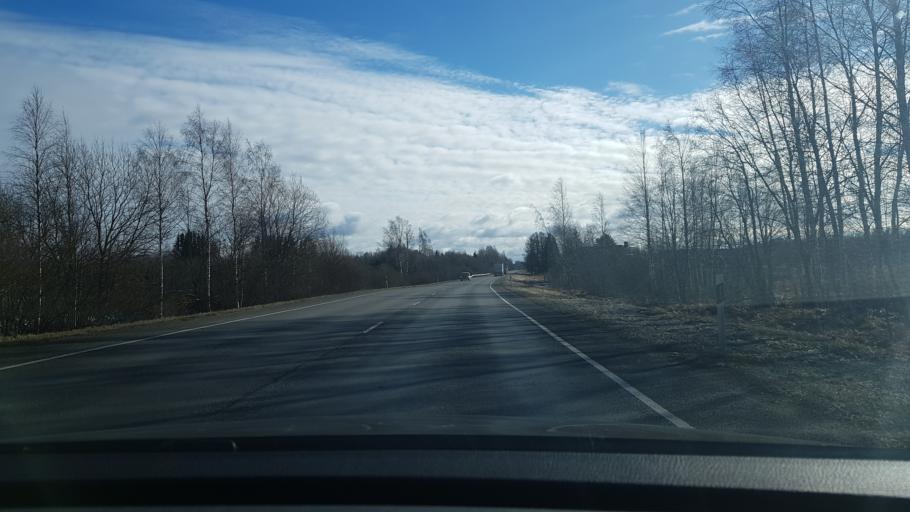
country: EE
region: Paernumaa
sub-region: Saarde vald
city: Kilingi-Nomme
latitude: 58.1869
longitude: 24.7872
